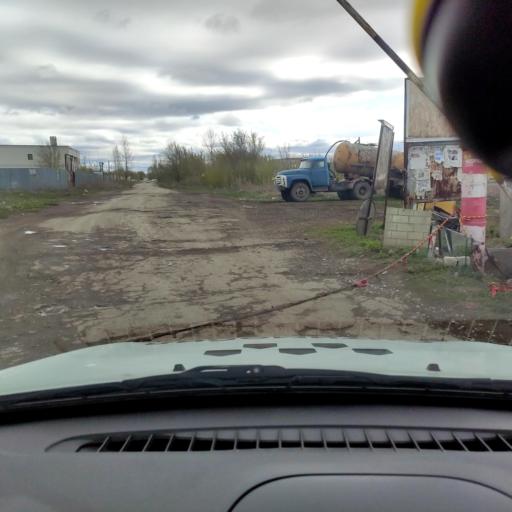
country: RU
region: Samara
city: Tol'yatti
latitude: 53.5815
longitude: 49.3146
